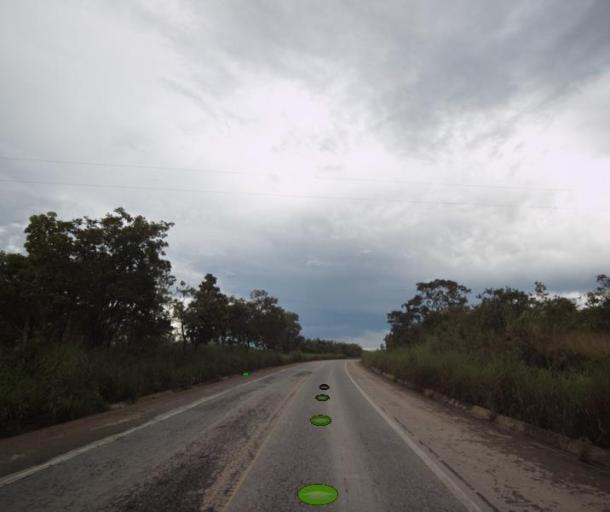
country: BR
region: Goias
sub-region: Porangatu
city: Porangatu
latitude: -13.5566
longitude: -49.0640
